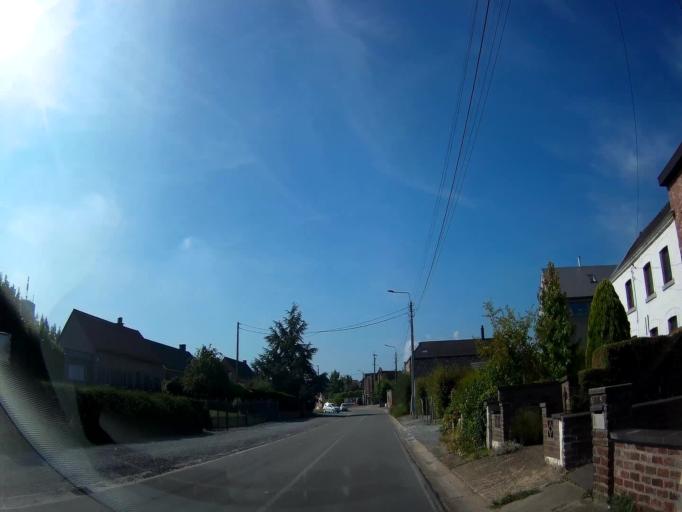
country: BE
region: Wallonia
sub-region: Province de Liege
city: Verlaine
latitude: 50.5934
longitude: 5.3419
